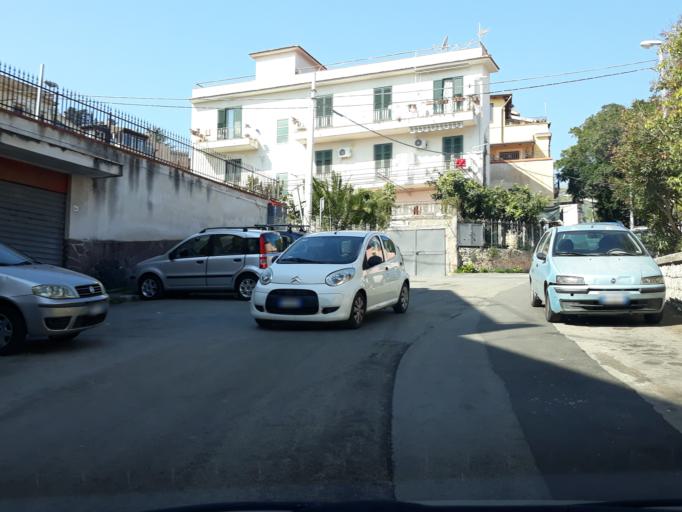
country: IT
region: Sicily
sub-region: Palermo
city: Piano dei Geli
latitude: 38.1091
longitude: 13.3047
